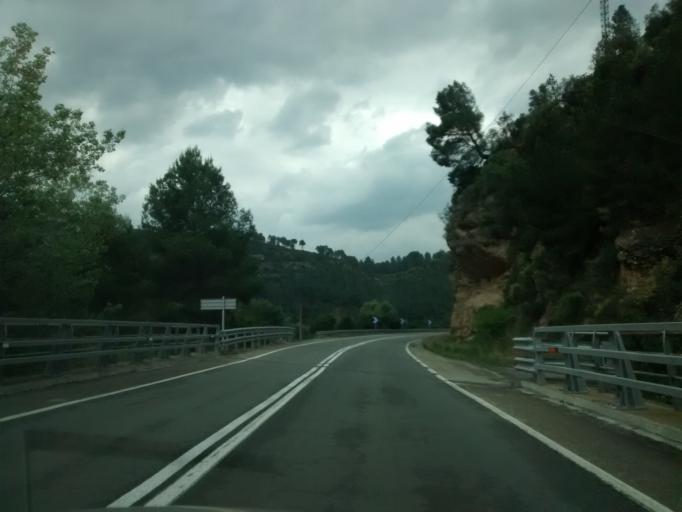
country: ES
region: Catalonia
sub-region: Provincia de Tarragona
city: Benifallet
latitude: 40.9620
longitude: 0.5087
